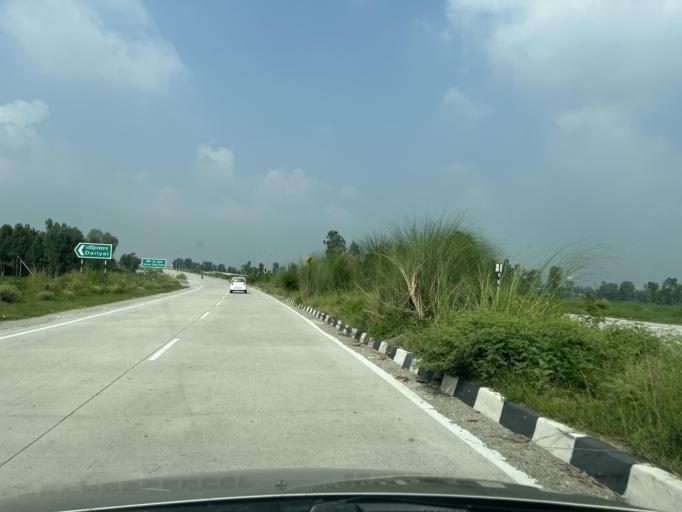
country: IN
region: Uttarakhand
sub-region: Udham Singh Nagar
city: Kashipur
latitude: 29.1667
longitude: 78.9817
